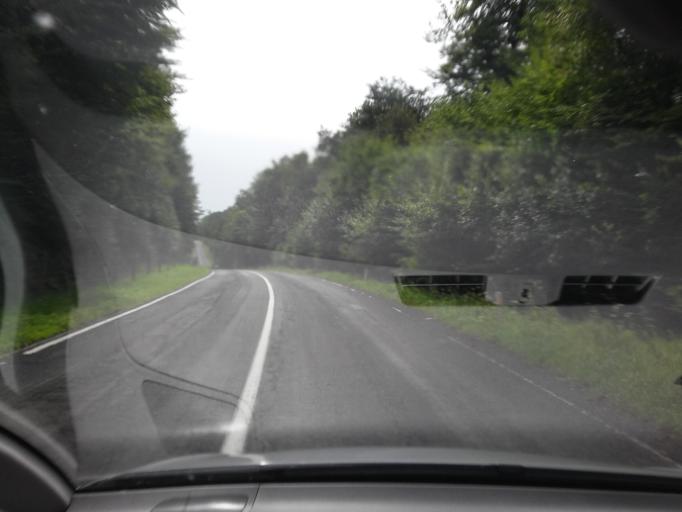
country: BE
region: Wallonia
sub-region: Province du Luxembourg
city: Chiny
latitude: 49.7758
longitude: 5.3508
